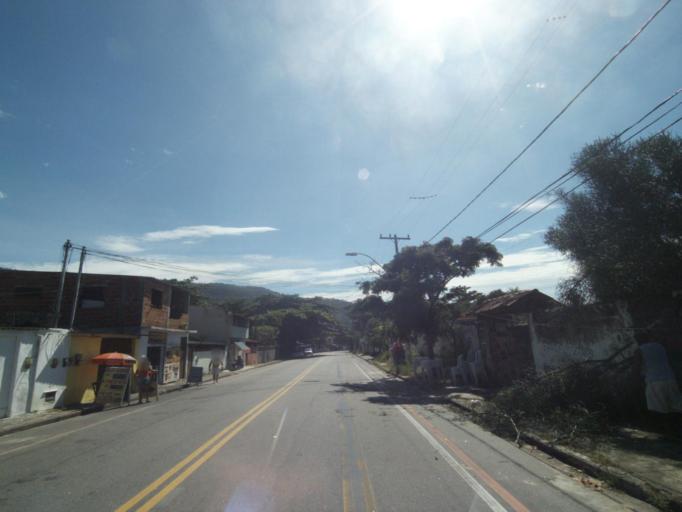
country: BR
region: Rio de Janeiro
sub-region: Niteroi
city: Niteroi
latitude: -22.9519
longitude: -43.0973
